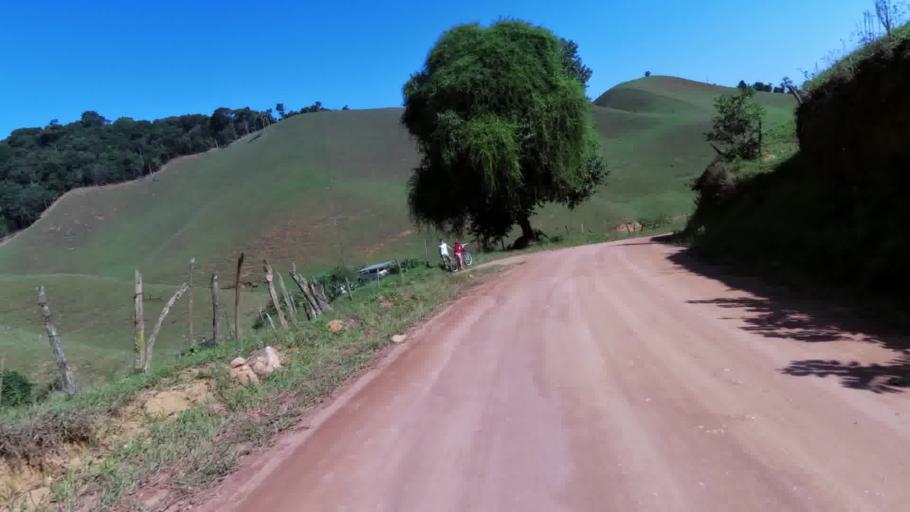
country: BR
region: Espirito Santo
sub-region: Alfredo Chaves
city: Alfredo Chaves
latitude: -20.5673
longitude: -40.7776
